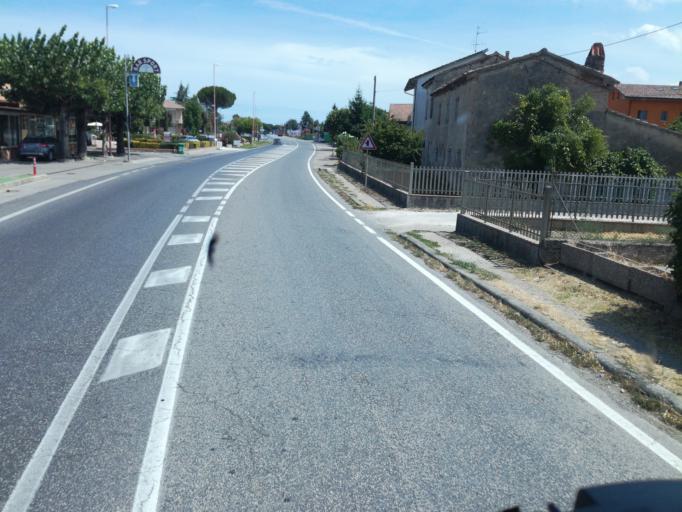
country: IT
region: Emilia-Romagna
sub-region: Forli-Cesena
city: Gambettola
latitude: 44.1073
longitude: 12.3262
